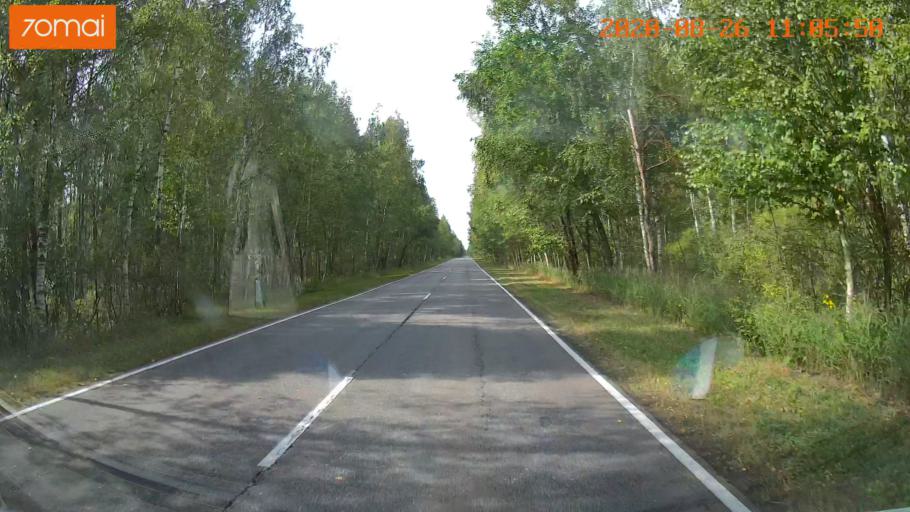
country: RU
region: Rjazan
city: Izhevskoye
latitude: 54.5257
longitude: 41.1624
